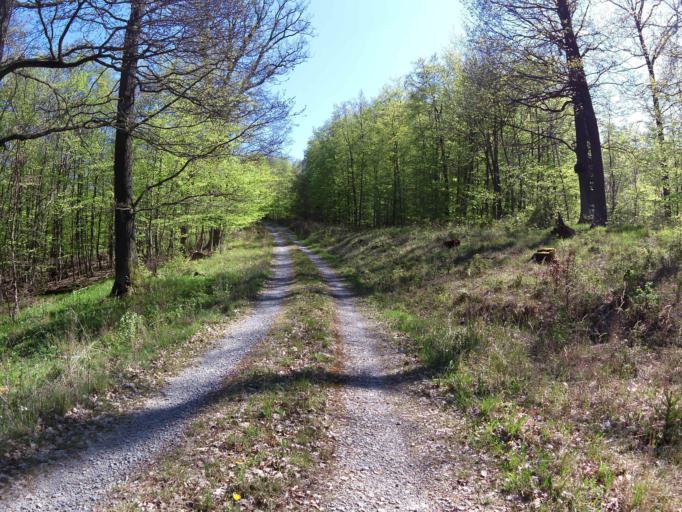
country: DE
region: Thuringia
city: Wolfsburg-Unkeroda
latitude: 50.9708
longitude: 10.2478
